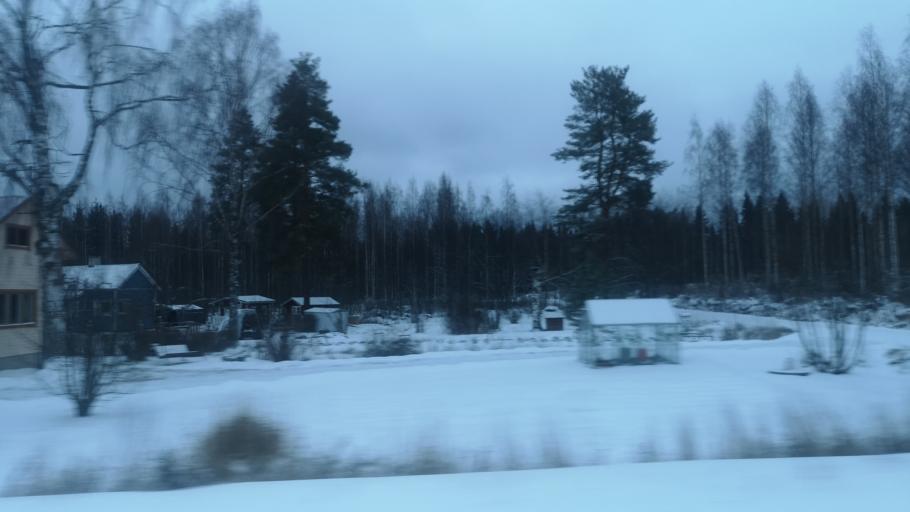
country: FI
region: Southern Savonia
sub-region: Savonlinna
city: Enonkoski
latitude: 62.1071
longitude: 28.6301
